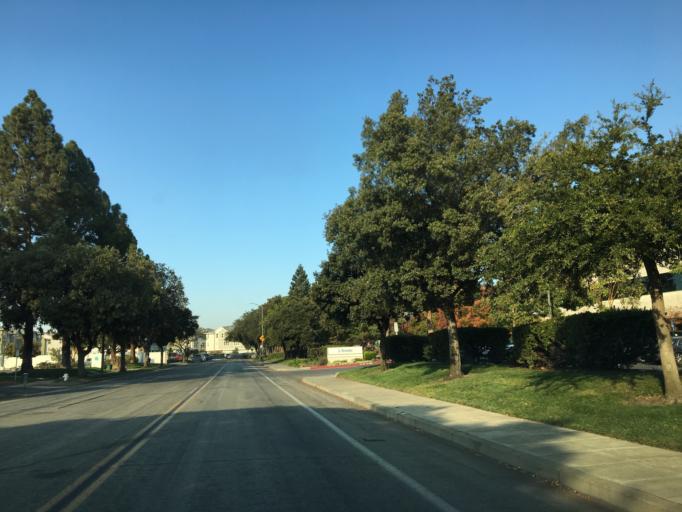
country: US
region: California
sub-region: Santa Clara County
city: Sunnyvale
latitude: 37.3843
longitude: -122.0071
